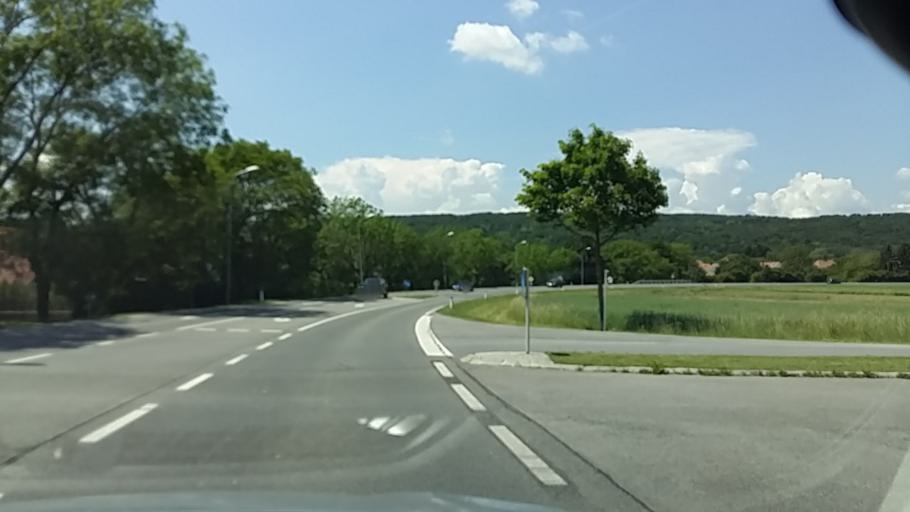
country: AT
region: Burgenland
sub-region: Politischer Bezirk Oberpullendorf
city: Oberpullendorf
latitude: 47.4818
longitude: 16.4884
